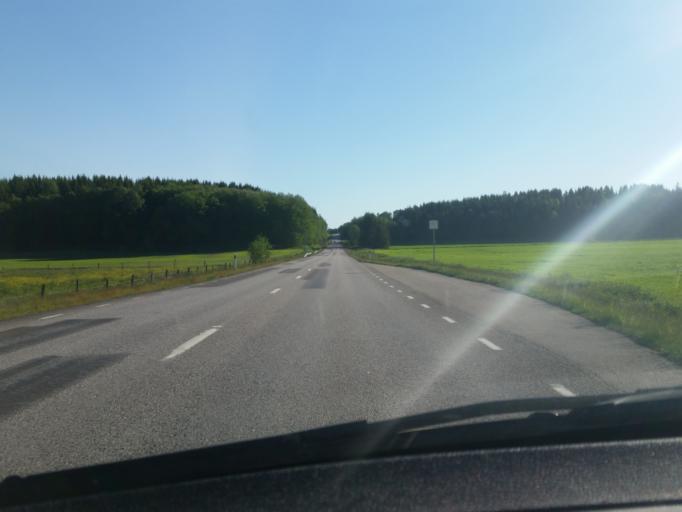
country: SE
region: Vaestra Goetaland
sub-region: Fargelanda Kommun
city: Faergelanda
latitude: 58.5818
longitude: 12.0222
